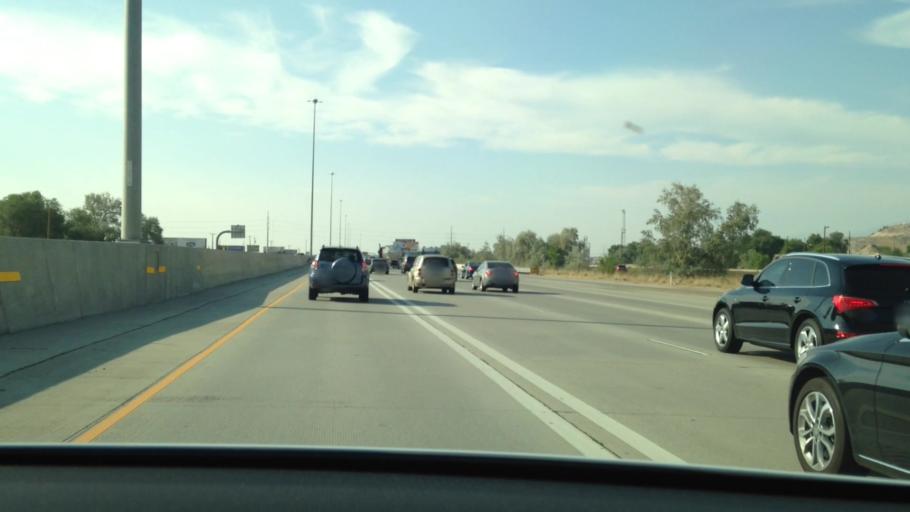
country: US
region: Utah
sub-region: Salt Lake County
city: Salt Lake City
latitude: 40.7972
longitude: -111.9202
